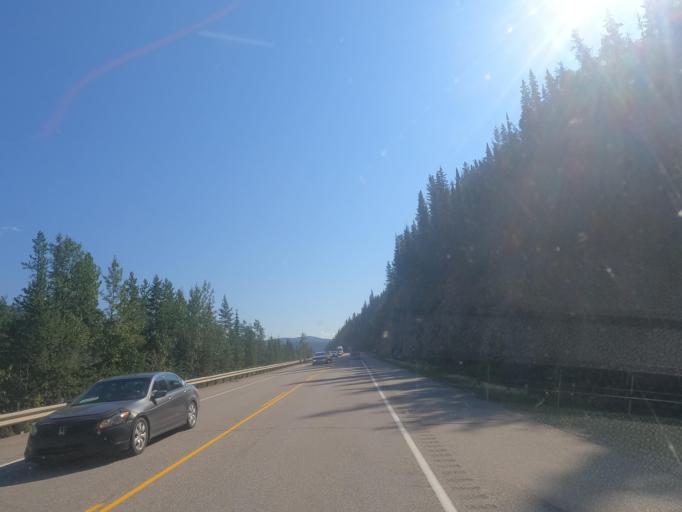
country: CA
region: Alberta
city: Jasper Park Lodge
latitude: 52.8726
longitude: -118.2967
